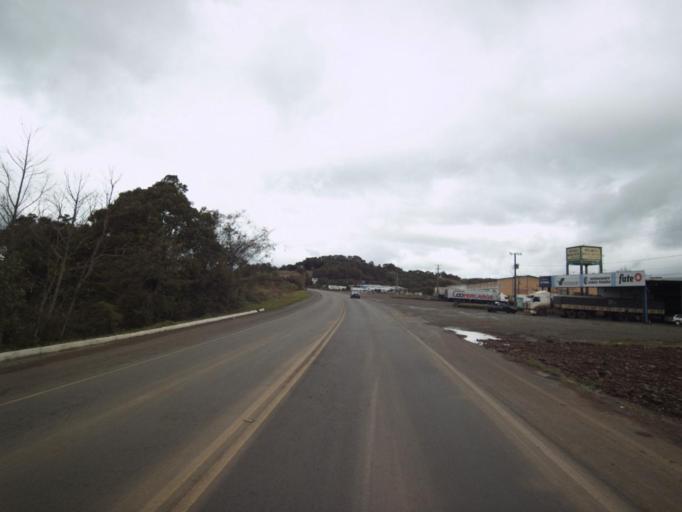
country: BR
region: Santa Catarina
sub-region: Concordia
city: Concordia
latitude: -27.2546
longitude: -51.9540
